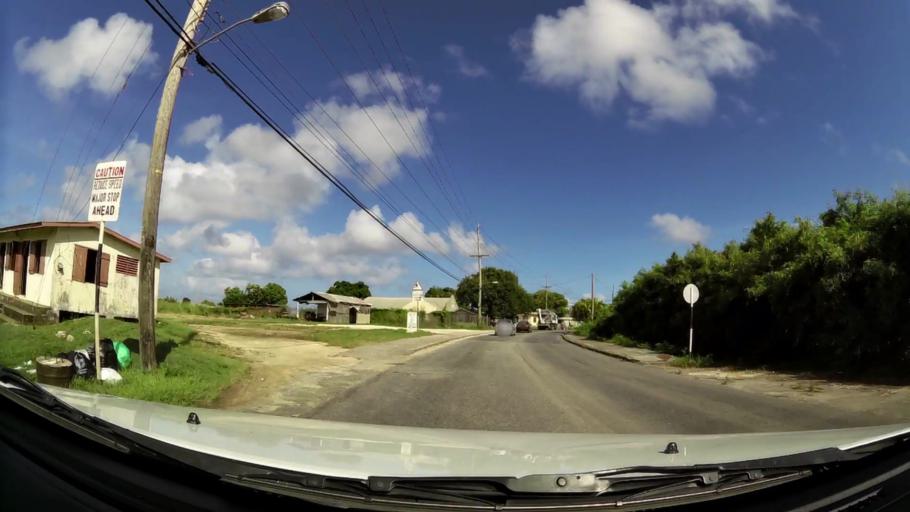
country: BB
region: Saint Lucy
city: Checker Hall
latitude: 13.2631
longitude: -59.6228
